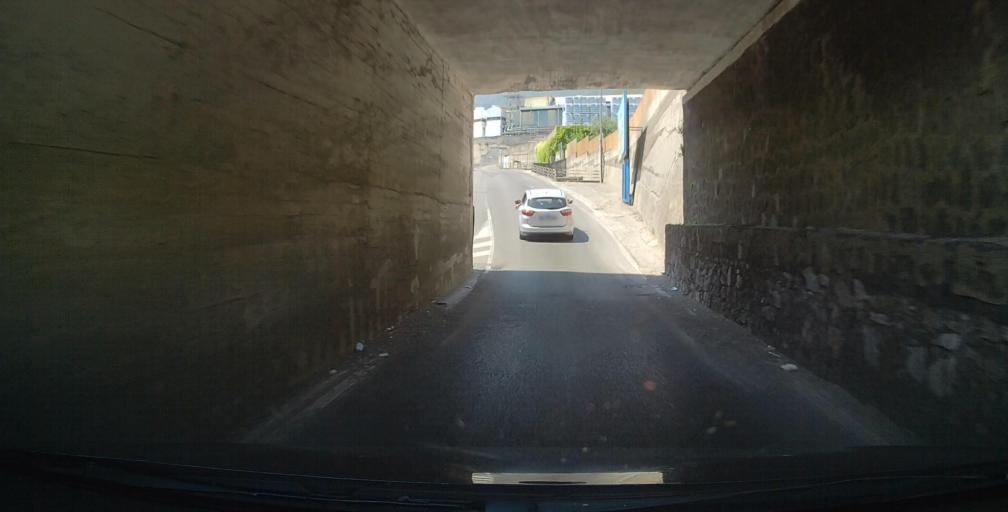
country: IT
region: Campania
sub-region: Provincia di Salerno
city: Cava De Tirreni
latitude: 40.7190
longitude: 14.6964
